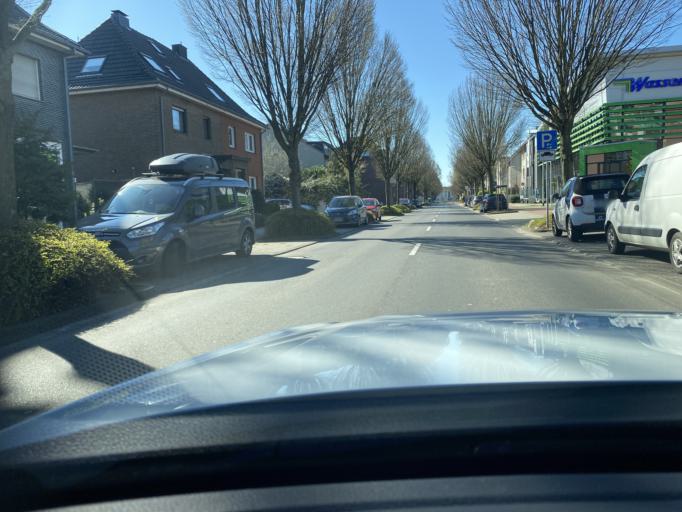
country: DE
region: North Rhine-Westphalia
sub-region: Regierungsbezirk Dusseldorf
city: Grevenbroich
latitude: 51.0962
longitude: 6.5826
